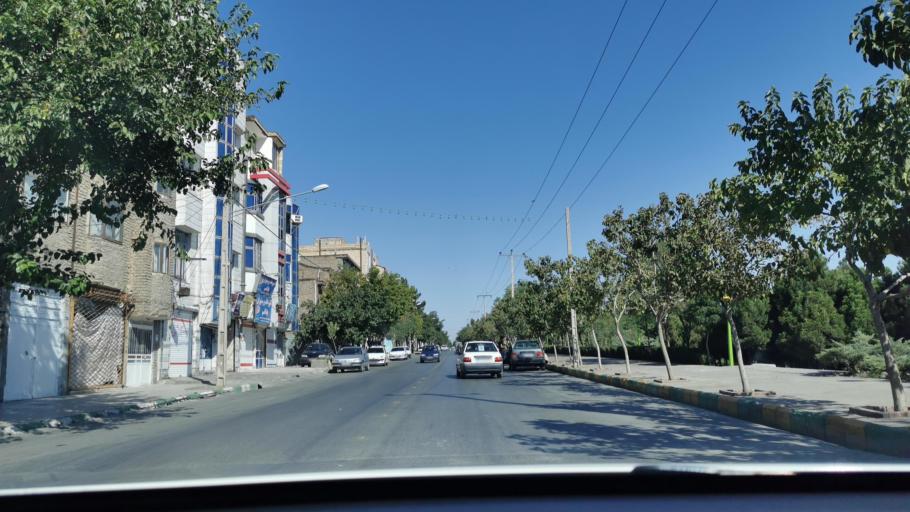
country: IR
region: Razavi Khorasan
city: Mashhad
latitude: 36.3325
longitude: 59.6421
